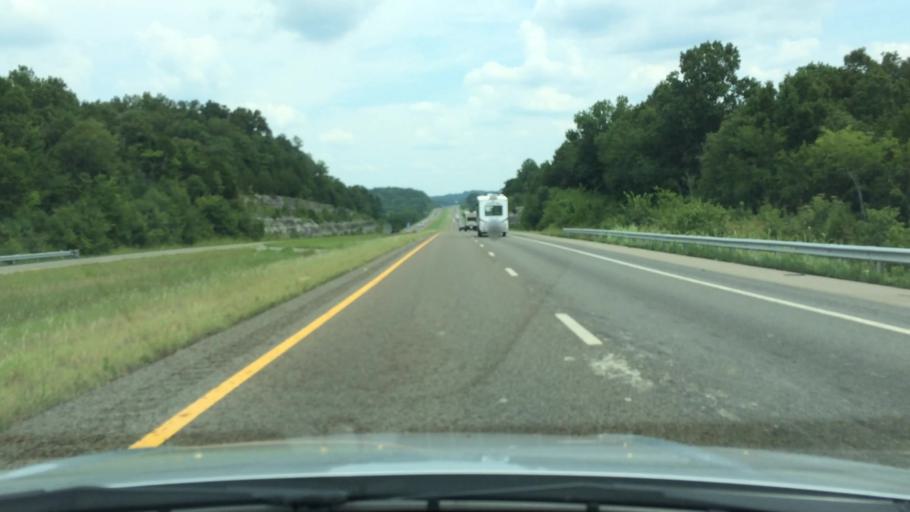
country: US
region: Tennessee
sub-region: Maury County
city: Columbia
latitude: 35.5960
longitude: -86.9019
